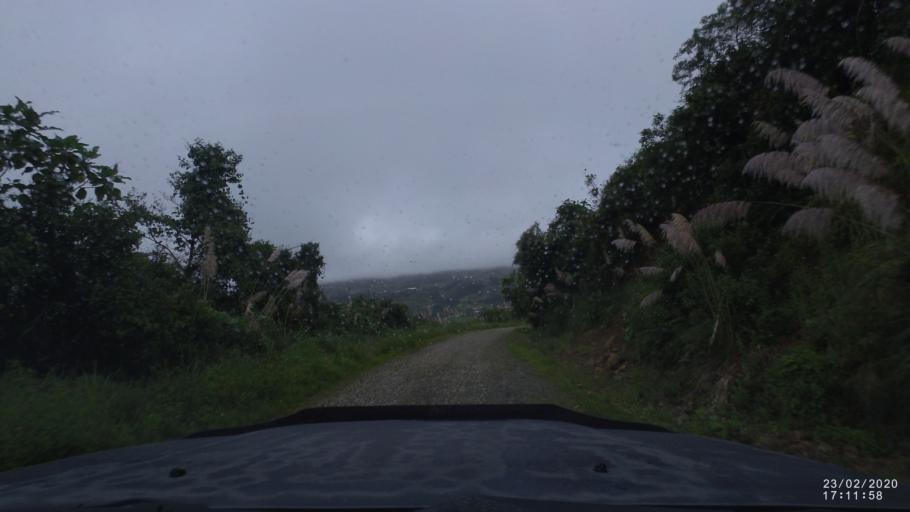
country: BO
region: Cochabamba
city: Colomi
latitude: -17.1332
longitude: -65.9434
